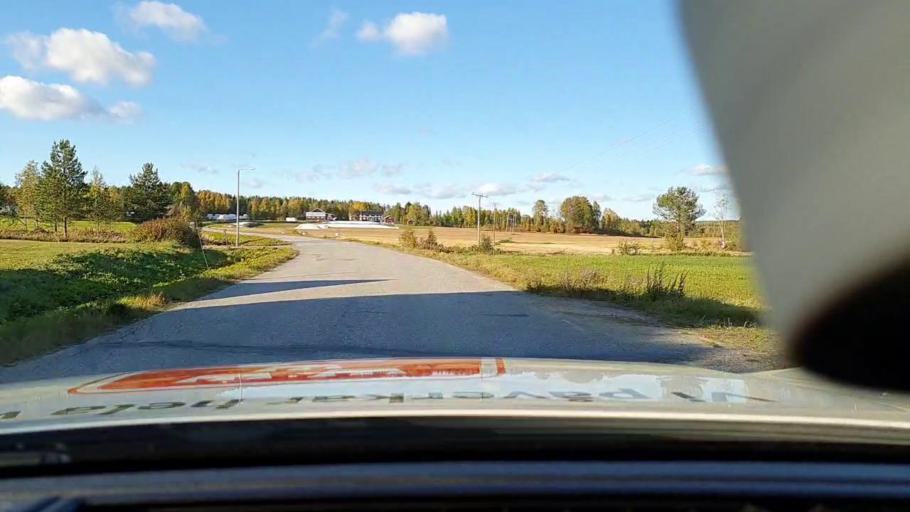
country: SE
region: Norrbotten
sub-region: Pitea Kommun
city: Norrfjarden
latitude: 65.5233
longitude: 21.4919
